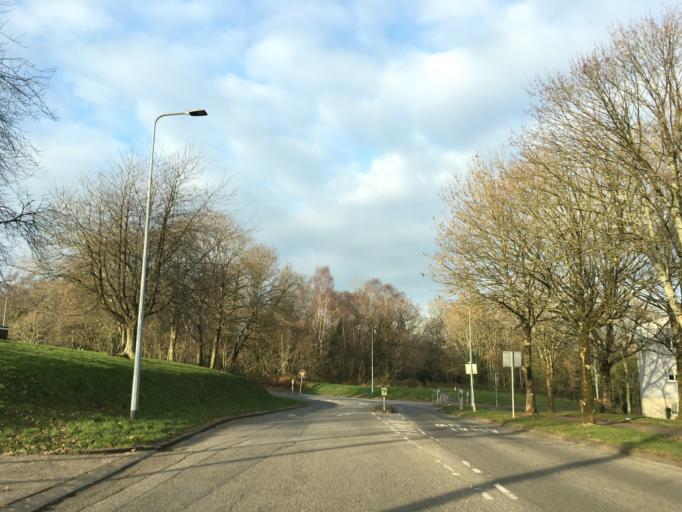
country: GB
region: Wales
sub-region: Cardiff
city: Cardiff
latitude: 51.5179
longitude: -3.1515
